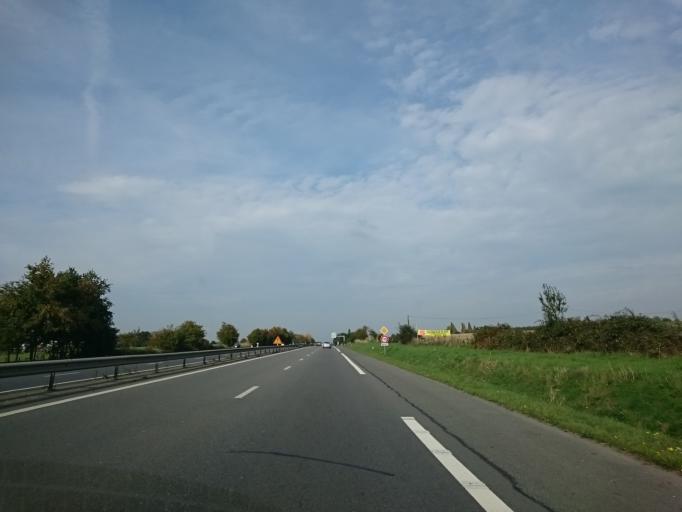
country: FR
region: Brittany
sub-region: Departement d'Ille-et-Vilaine
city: Orgeres
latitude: 48.0134
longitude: -1.6914
